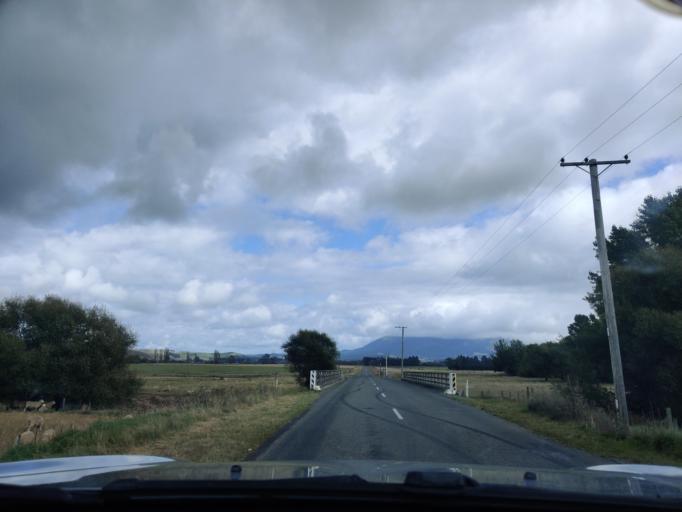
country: NZ
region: Canterbury
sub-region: Hurunui District
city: Amberley
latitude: -43.1274
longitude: 172.6840
